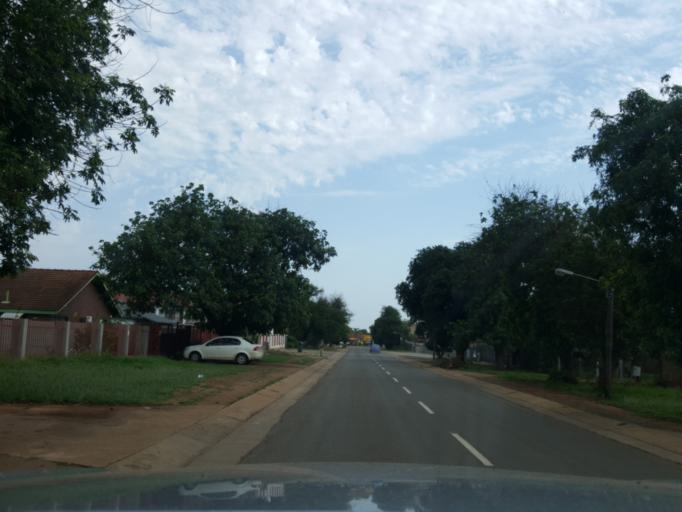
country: SZ
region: Hhohho
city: Ntfonjeni
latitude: -25.4974
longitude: 31.5088
